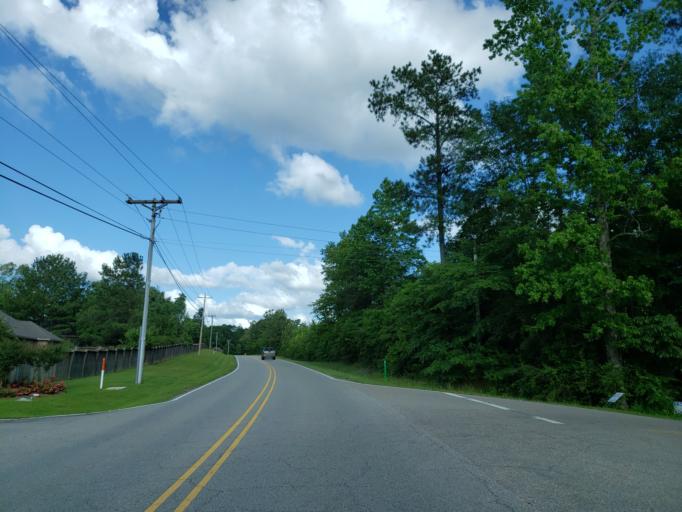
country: US
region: Mississippi
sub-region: Lamar County
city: West Hattiesburg
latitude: 31.2887
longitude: -89.4461
